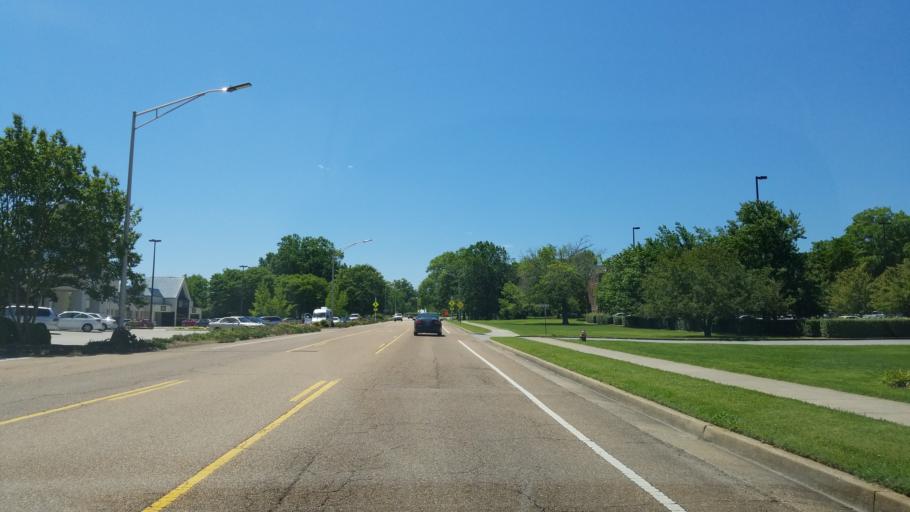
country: US
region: Tennessee
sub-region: Hamilton County
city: Collegedale
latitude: 35.0503
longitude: -85.0490
